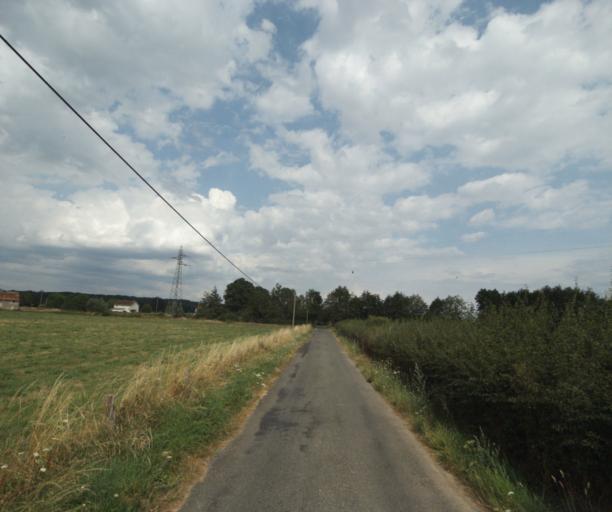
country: FR
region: Bourgogne
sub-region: Departement de Saone-et-Loire
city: Gueugnon
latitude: 46.6128
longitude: 4.0738
